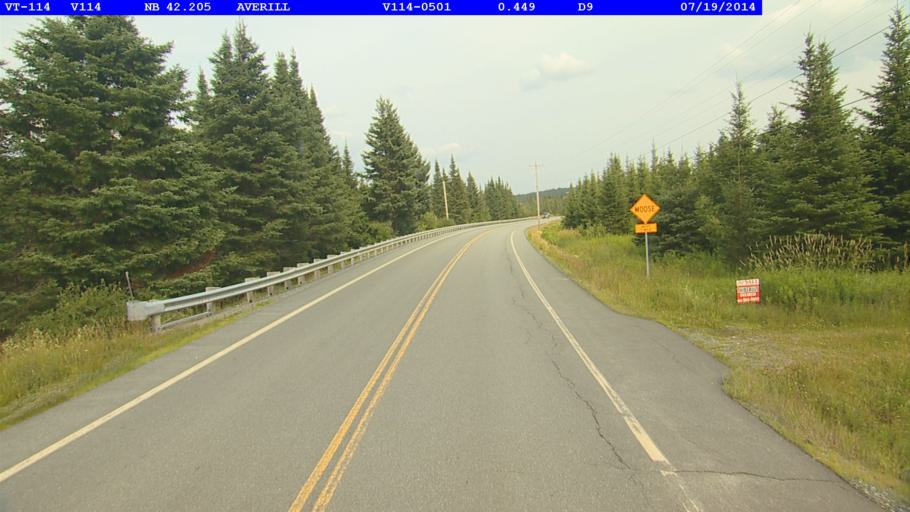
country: CA
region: Quebec
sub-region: Estrie
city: Coaticook
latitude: 45.0031
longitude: -71.7014
